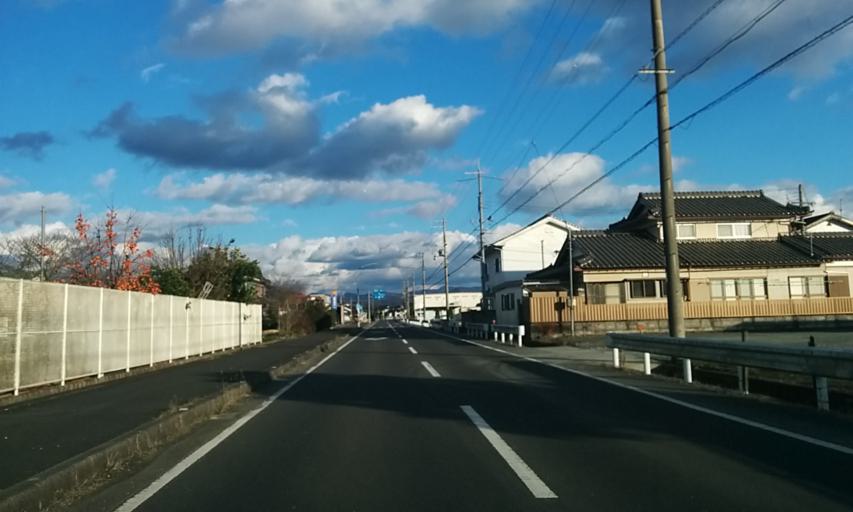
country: JP
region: Kyoto
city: Ayabe
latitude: 35.3118
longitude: 135.2151
